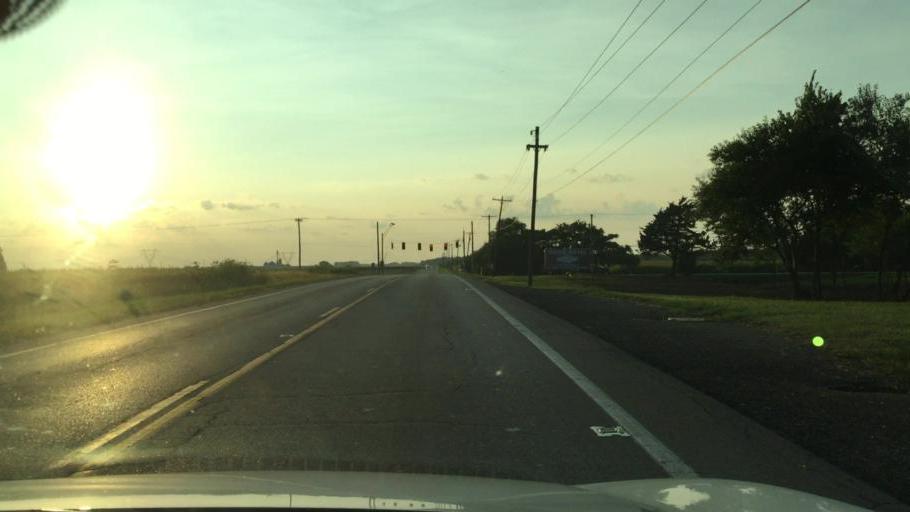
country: US
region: Ohio
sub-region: Madison County
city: West Jefferson
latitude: 39.9657
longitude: -83.3610
